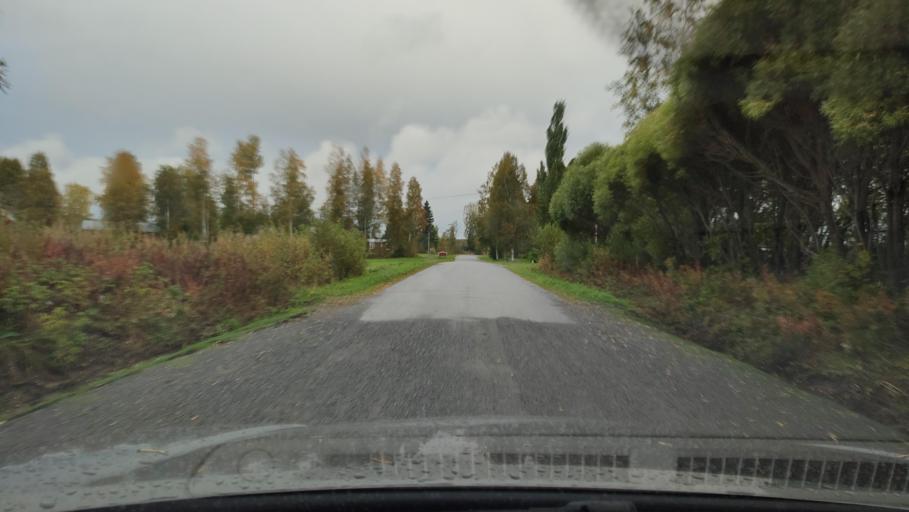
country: FI
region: Southern Ostrobothnia
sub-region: Suupohja
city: Karijoki
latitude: 62.2260
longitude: 21.6298
